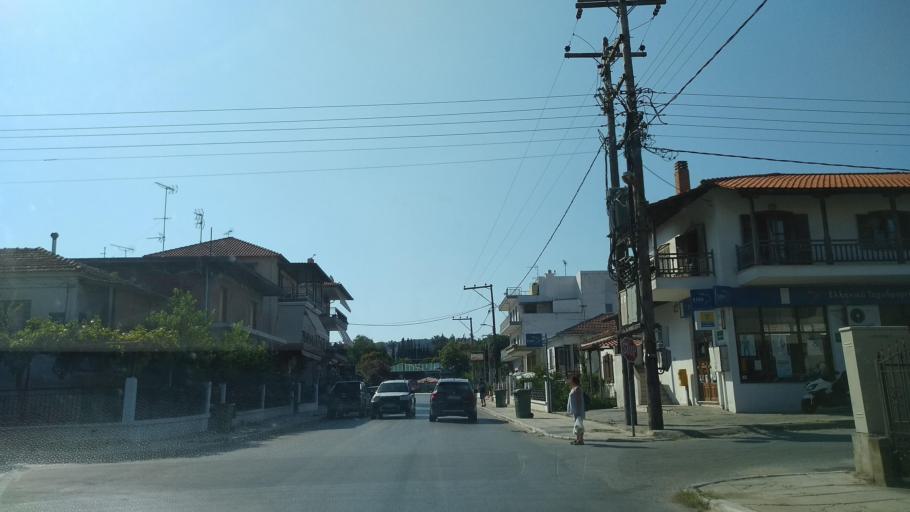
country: GR
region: Central Macedonia
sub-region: Nomos Chalkidikis
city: Ierissos
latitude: 40.3983
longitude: 23.8739
